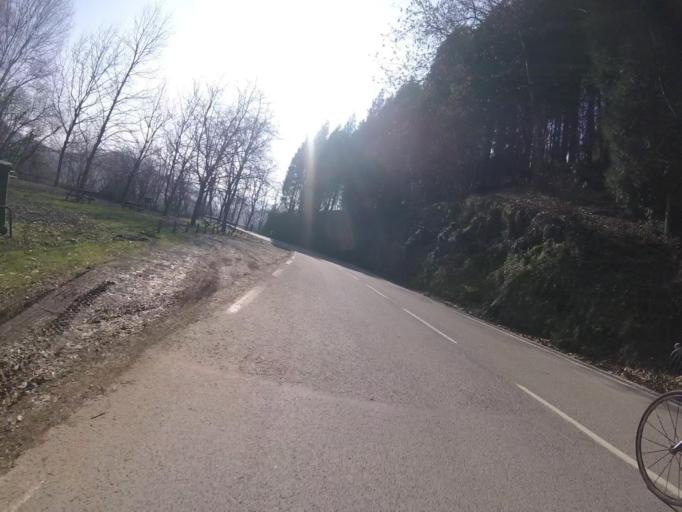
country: ES
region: Navarre
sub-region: Provincia de Navarra
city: Bera
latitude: 43.2952
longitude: -1.6911
